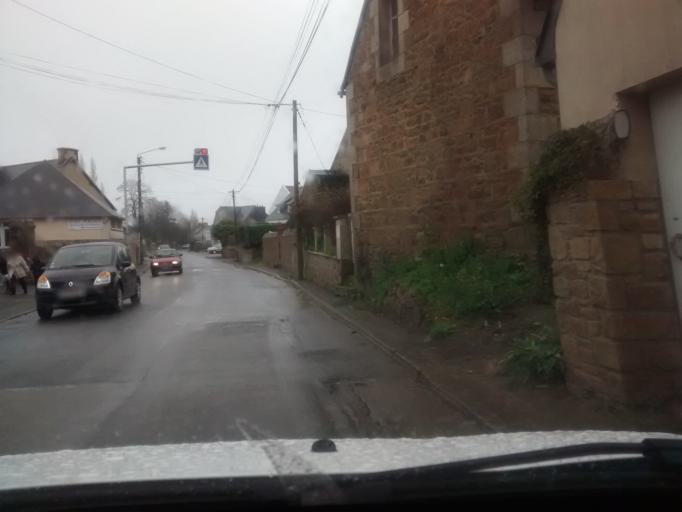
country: FR
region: Brittany
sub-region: Departement des Cotes-d'Armor
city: Penvenan
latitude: 48.8151
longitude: -3.2969
